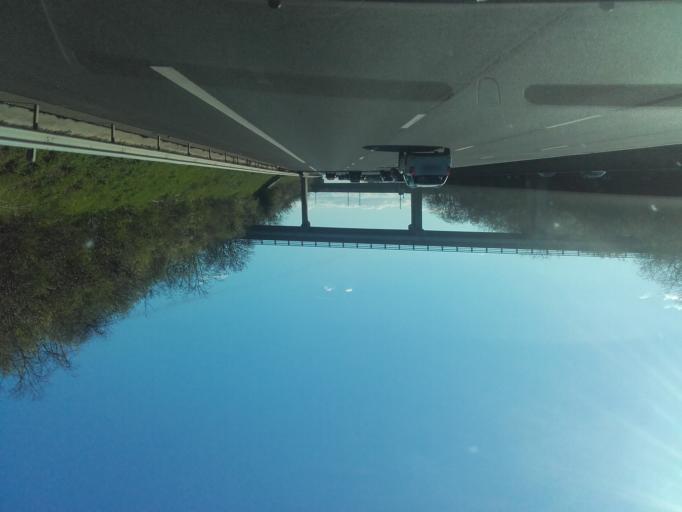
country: FR
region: Rhone-Alpes
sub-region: Departement de l'Isere
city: Grenay
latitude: 45.6589
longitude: 5.0777
